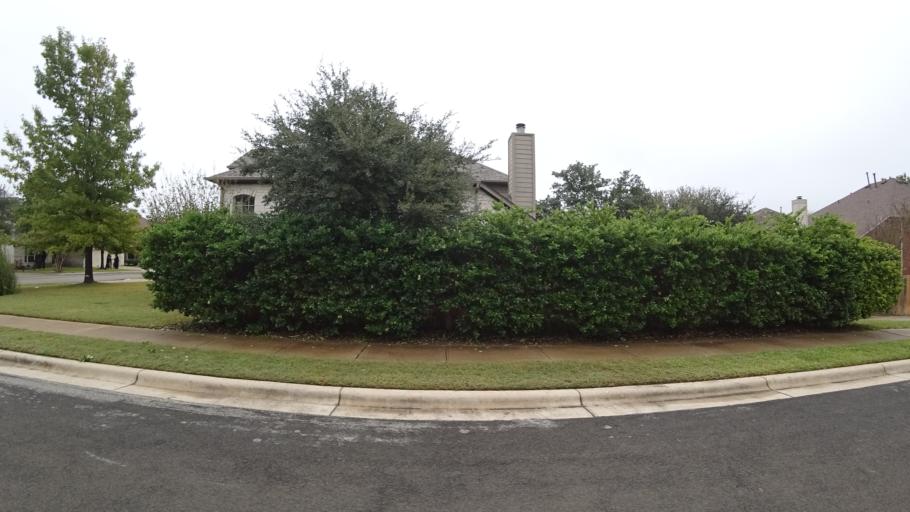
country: US
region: Texas
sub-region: Travis County
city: Shady Hollow
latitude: 30.1908
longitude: -97.8687
